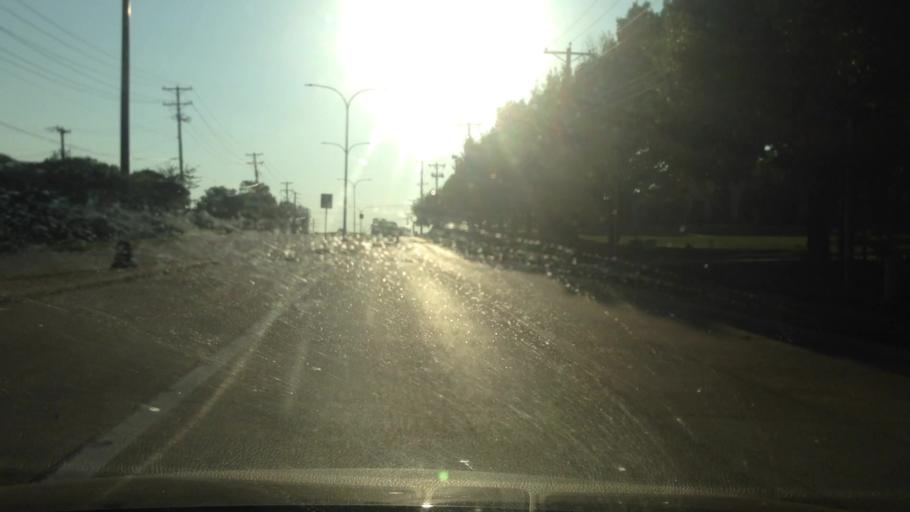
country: US
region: Texas
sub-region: Tarrant County
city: Dalworthington Gardens
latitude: 32.6824
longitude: -97.1836
